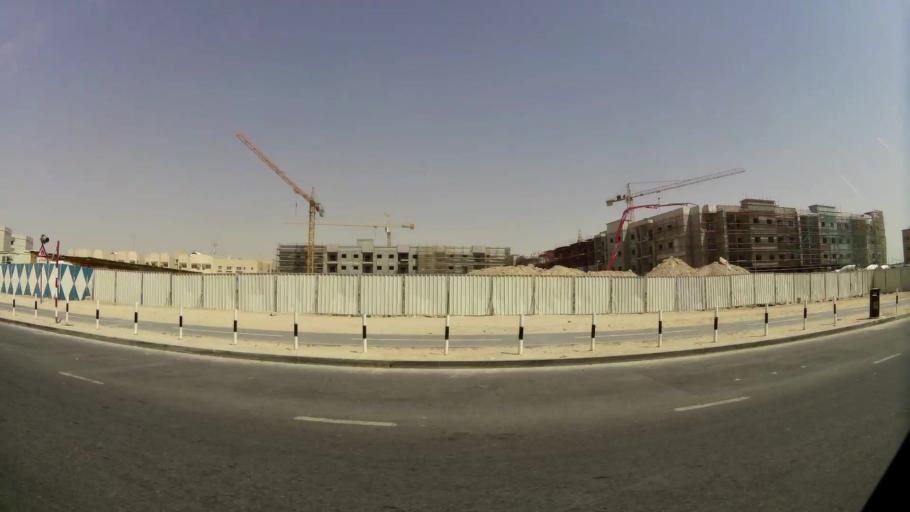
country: AE
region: Dubai
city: Dubai
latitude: 25.1527
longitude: 55.2450
